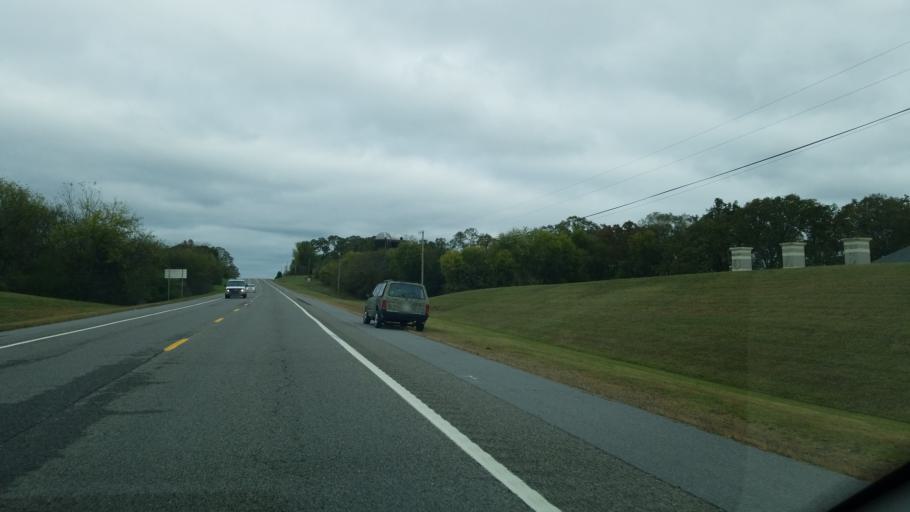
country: US
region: Tennessee
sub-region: Rhea County
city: Graysville
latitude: 35.3826
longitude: -85.0018
